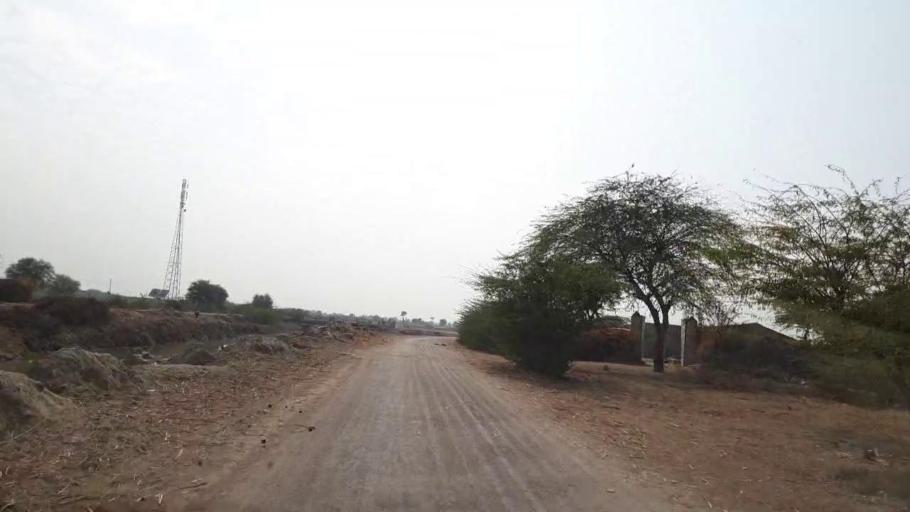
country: PK
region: Sindh
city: Mirpur Khas
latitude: 25.5425
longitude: 69.1618
